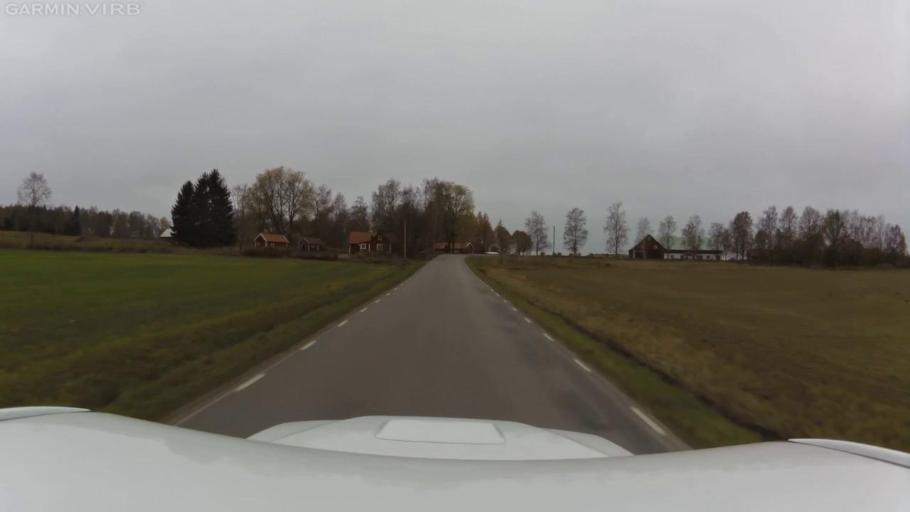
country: SE
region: OEstergoetland
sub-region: Linkopings Kommun
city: Vikingstad
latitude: 58.3656
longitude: 15.4231
